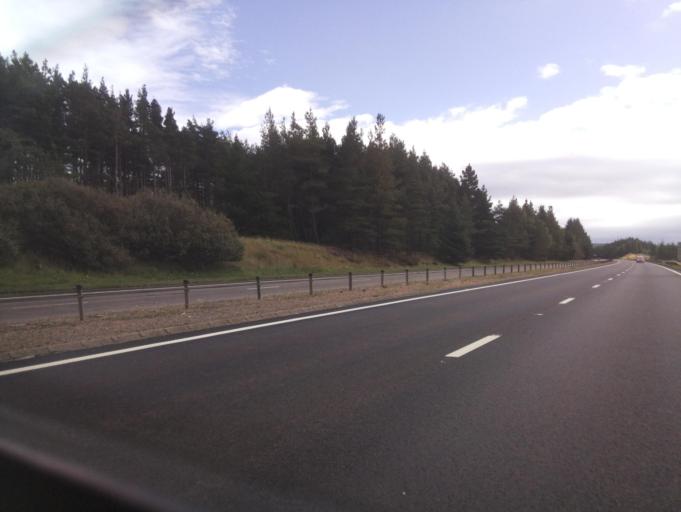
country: GB
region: Scotland
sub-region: Highland
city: Inverness
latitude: 57.4057
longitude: -4.1338
